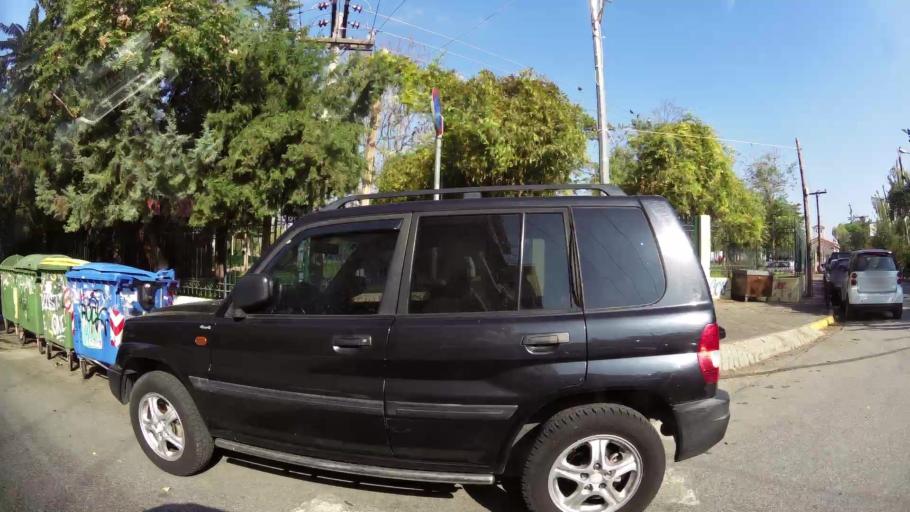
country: GR
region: Attica
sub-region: Nomarchia Athinas
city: Papagou
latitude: 37.9838
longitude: 23.7749
